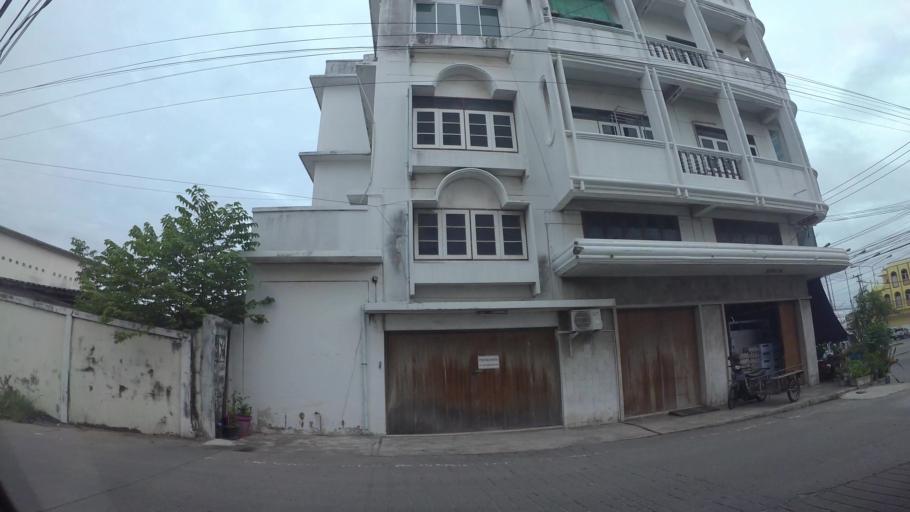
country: TH
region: Rayong
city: Rayong
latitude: 12.6614
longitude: 101.2709
